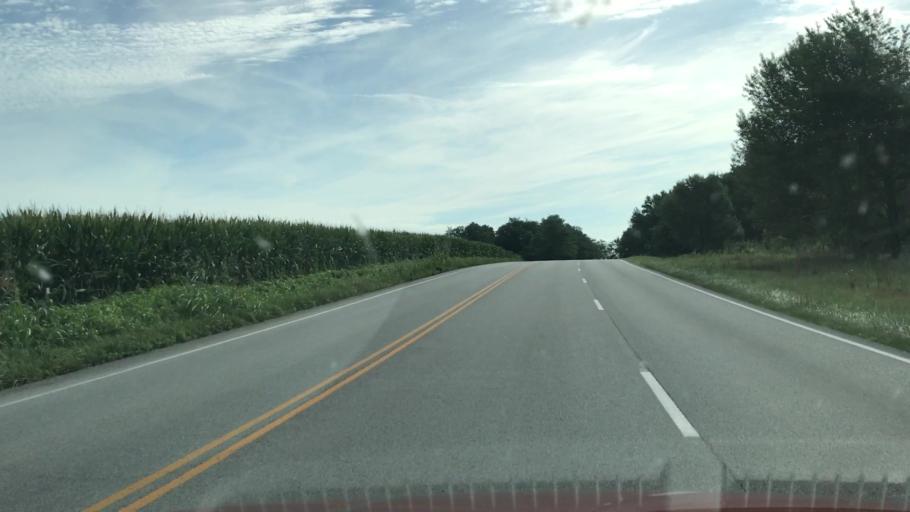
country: US
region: Kentucky
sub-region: Edmonson County
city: Brownsville
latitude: 37.0718
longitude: -86.2648
